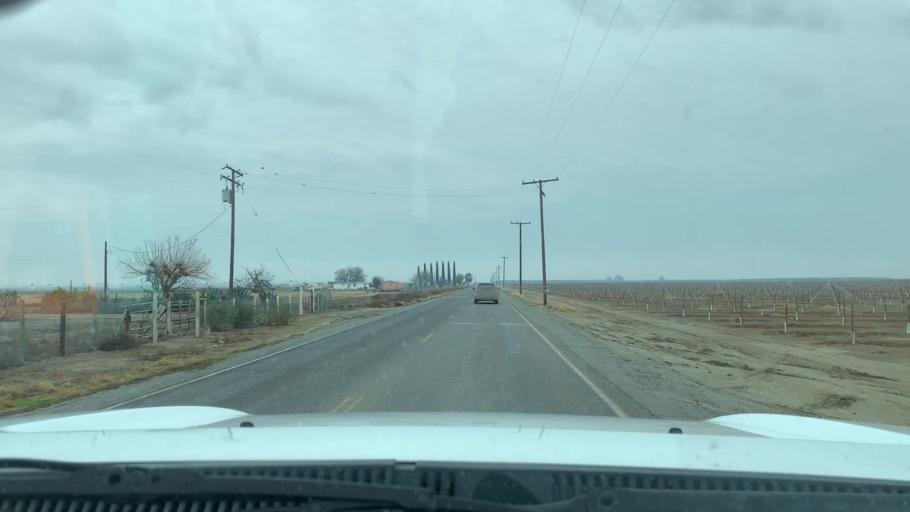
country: US
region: California
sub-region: Kern County
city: Delano
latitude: 35.7612
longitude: -119.3433
